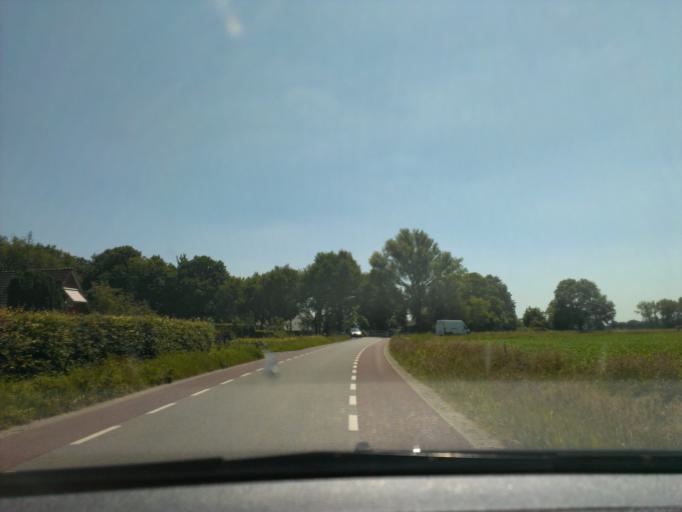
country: NL
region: Gelderland
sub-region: Gemeente Heerde
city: Heerde
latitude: 52.3764
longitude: 6.0508
